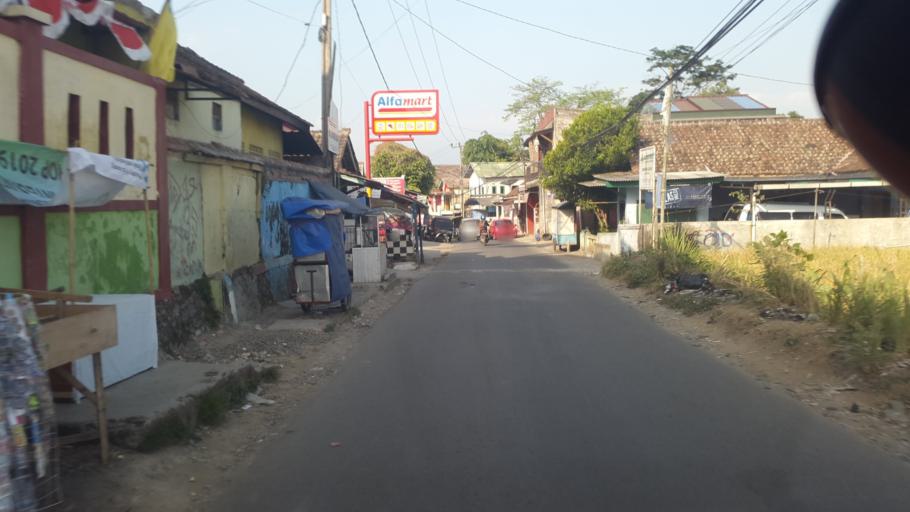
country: ID
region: West Java
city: Cicurug
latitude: -6.7980
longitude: 106.7409
